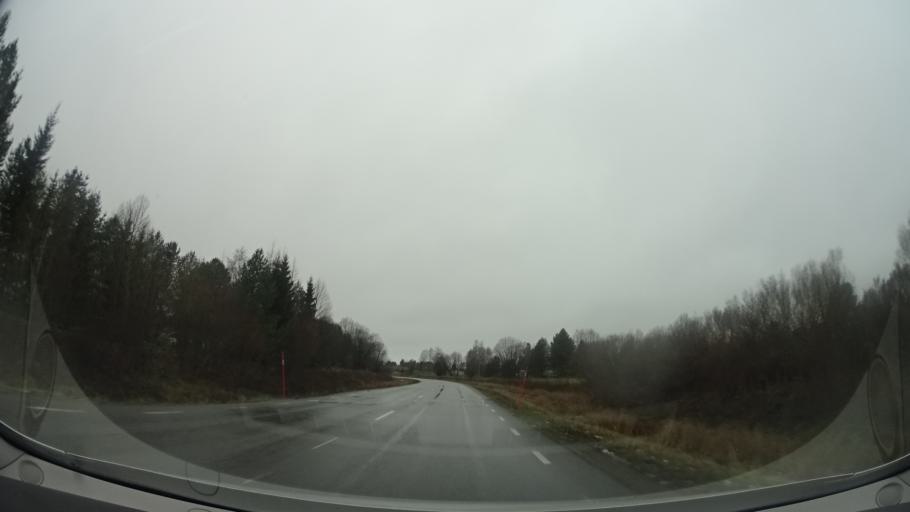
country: SE
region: Vaesterbotten
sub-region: Skelleftea Kommun
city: Kage
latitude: 64.8387
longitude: 20.9812
